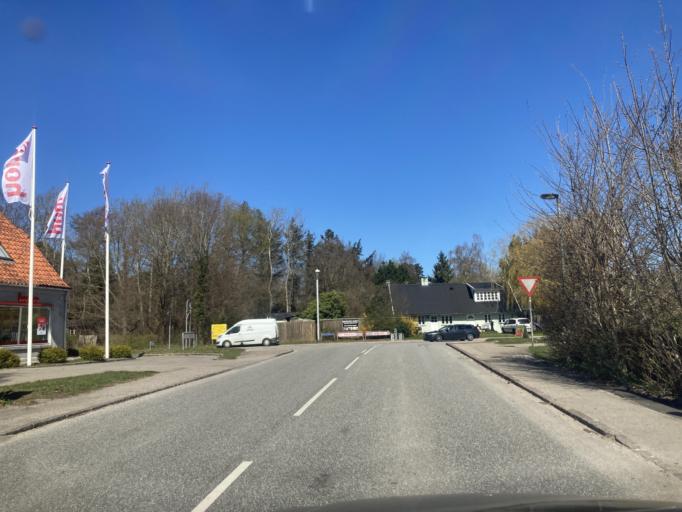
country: DK
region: Capital Region
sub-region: Gribskov Kommune
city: Graested
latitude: 56.1150
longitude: 12.2366
